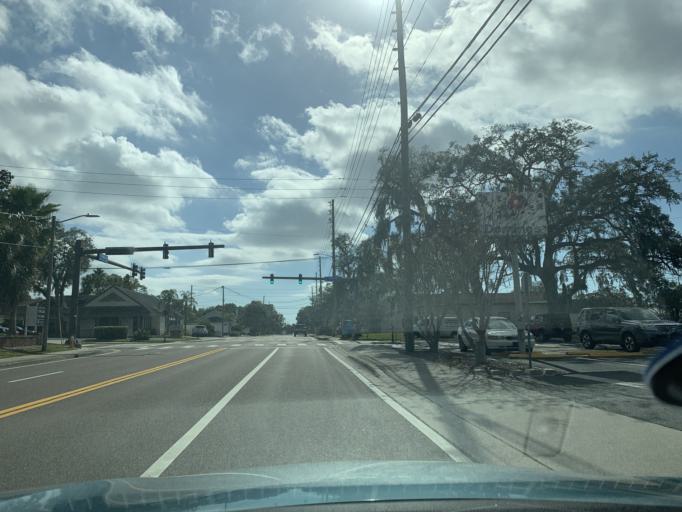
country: US
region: Florida
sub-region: Pinellas County
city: Clearwater
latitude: 27.9541
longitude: -82.7959
